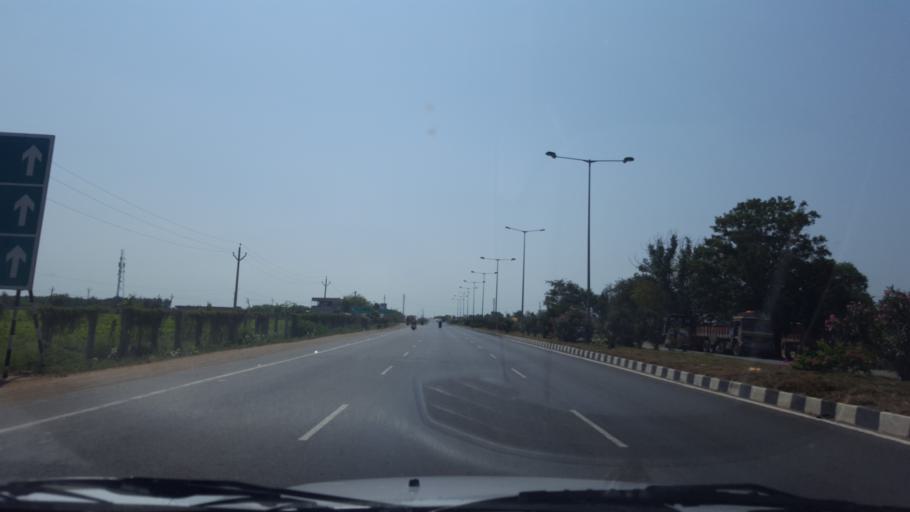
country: IN
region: Andhra Pradesh
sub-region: Prakasam
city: Addanki
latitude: 15.6646
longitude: 80.0154
